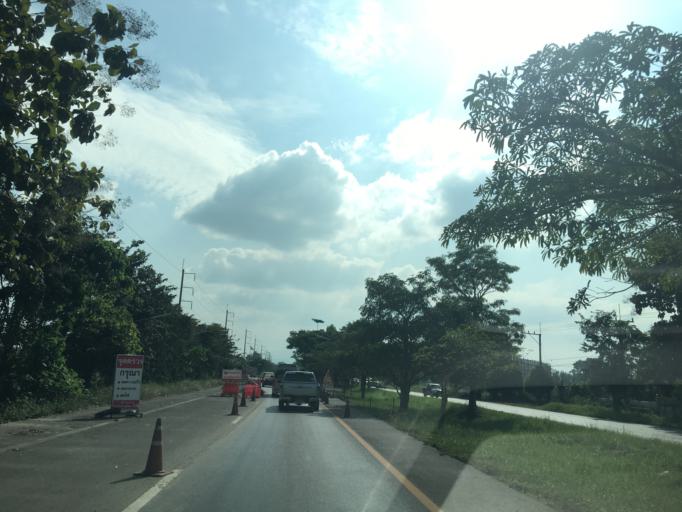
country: TH
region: Chiang Rai
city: Mae Lao
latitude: 19.7329
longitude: 99.7195
